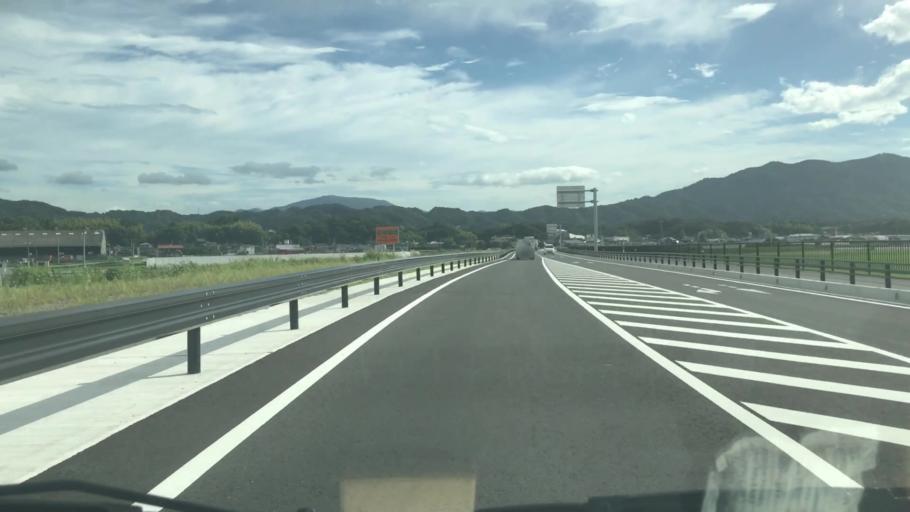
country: JP
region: Saga Prefecture
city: Takeocho-takeo
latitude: 33.2147
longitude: 130.0519
